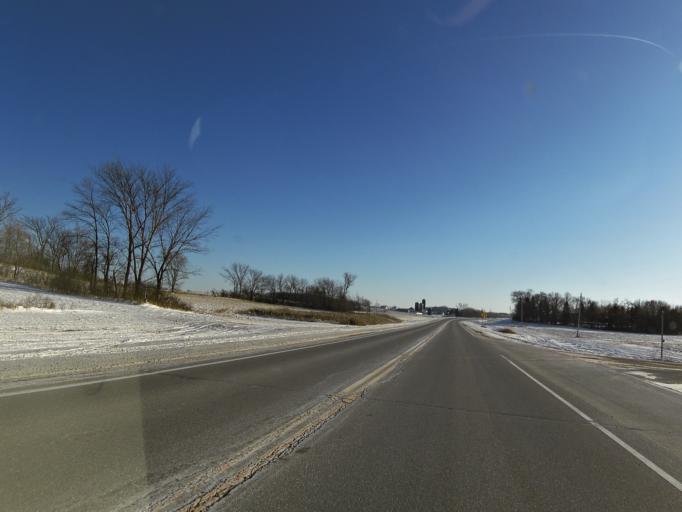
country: US
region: Minnesota
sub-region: Le Sueur County
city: New Prague
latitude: 44.5694
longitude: -93.5036
